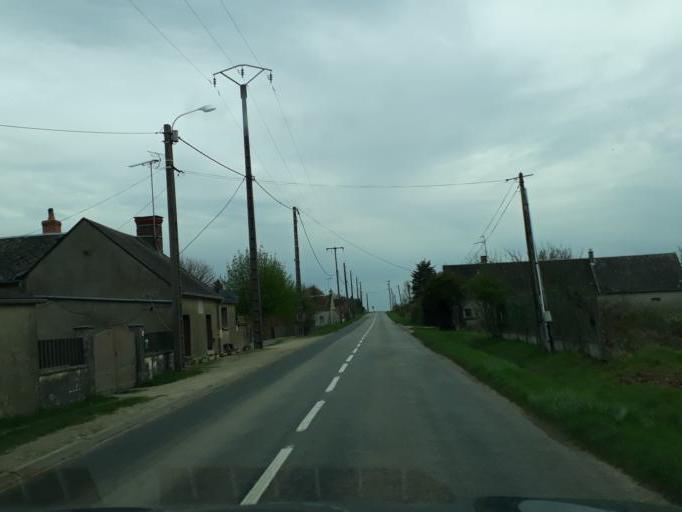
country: FR
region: Centre
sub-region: Departement du Loiret
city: Epieds-en-Beauce
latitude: 47.9125
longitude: 1.6075
